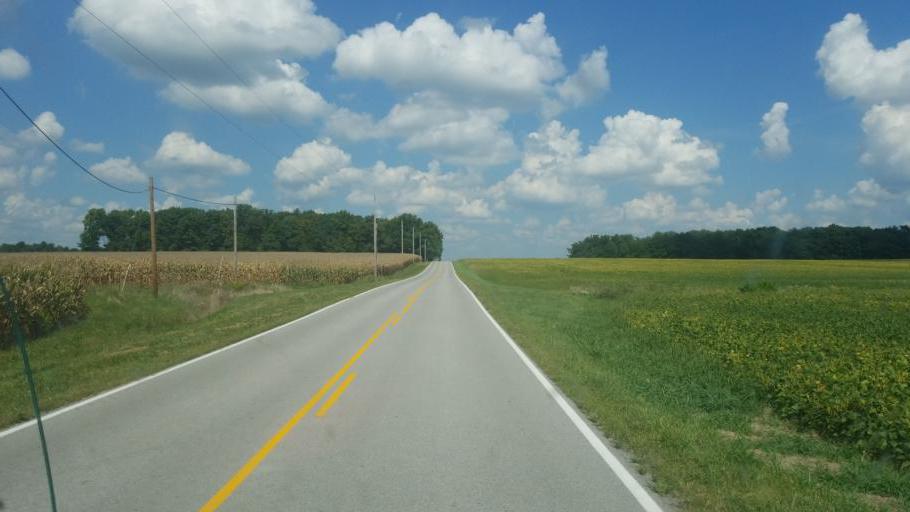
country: US
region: Ohio
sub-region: Hancock County
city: Arlington
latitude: 40.8638
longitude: -83.7274
